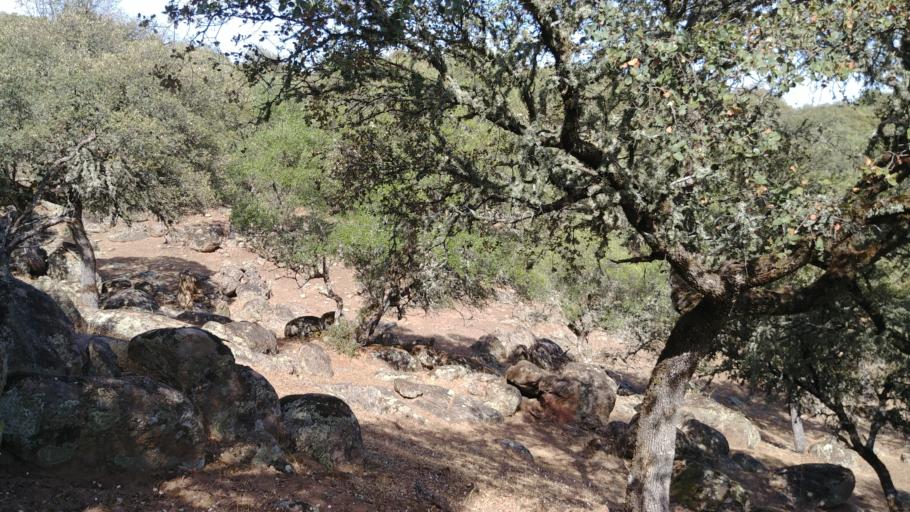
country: ES
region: Castille-La Mancha
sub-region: Province of Toledo
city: Navalcan
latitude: 40.0539
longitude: -5.1434
